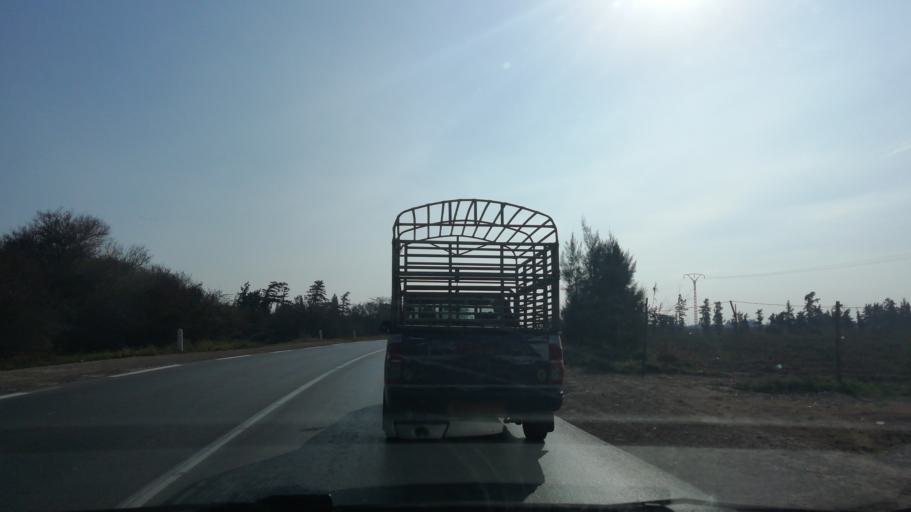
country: DZ
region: Mostaganem
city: Mostaganem
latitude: 35.7434
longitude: -0.0122
